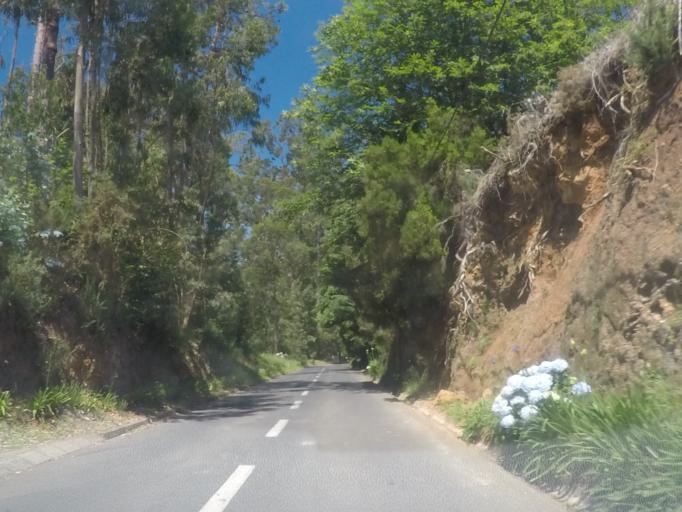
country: PT
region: Madeira
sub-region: Camara de Lobos
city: Curral das Freiras
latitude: 32.6870
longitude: -16.9798
